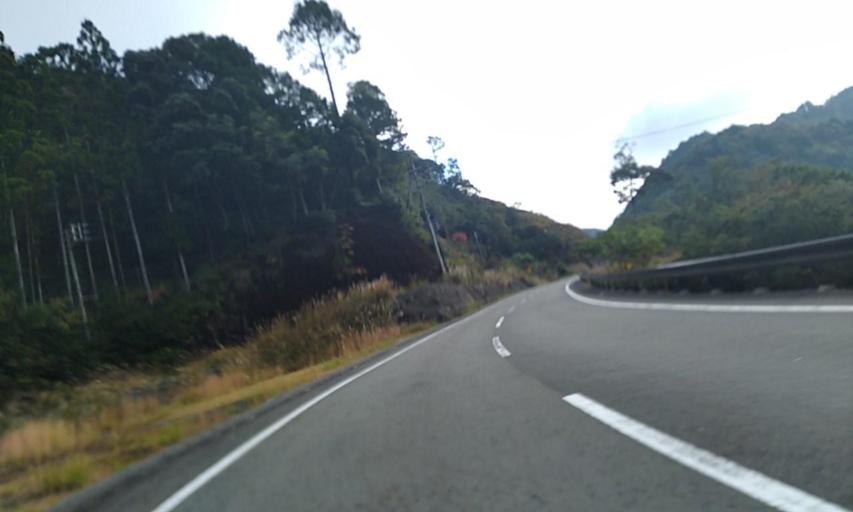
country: JP
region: Wakayama
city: Shingu
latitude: 33.8763
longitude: 135.8672
